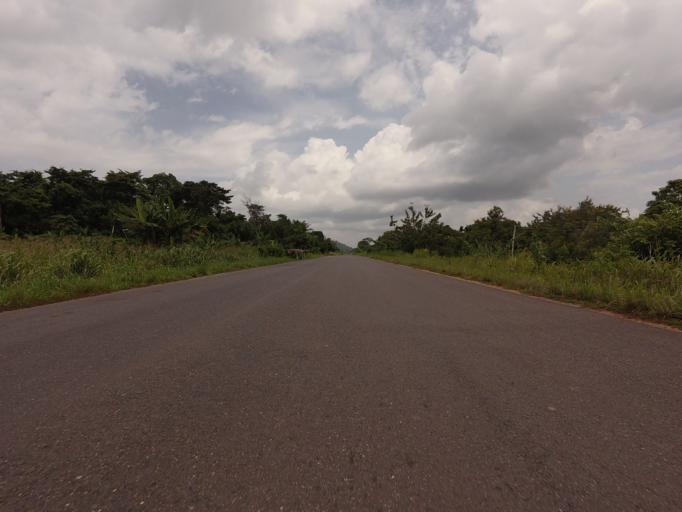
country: GH
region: Volta
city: Ho
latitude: 6.4948
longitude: 0.2025
